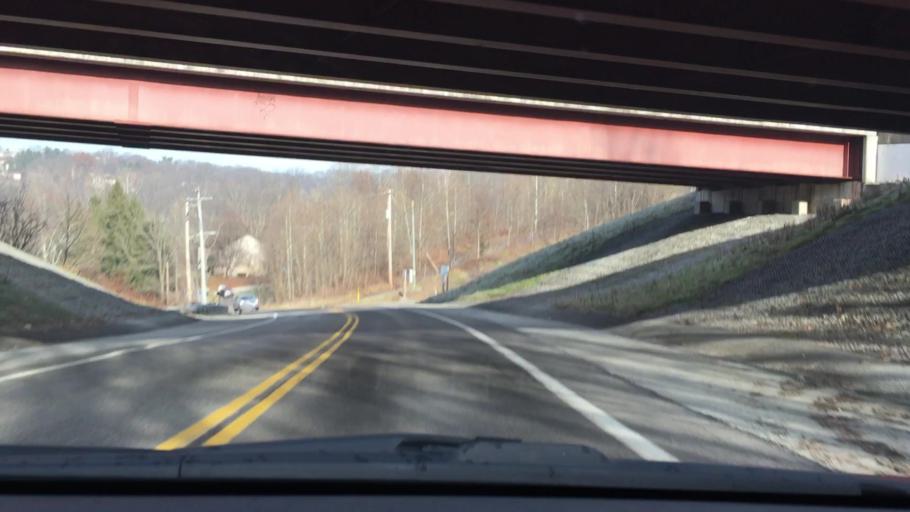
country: US
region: Pennsylvania
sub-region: Allegheny County
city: Jefferson Hills
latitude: 40.2774
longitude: -79.9496
